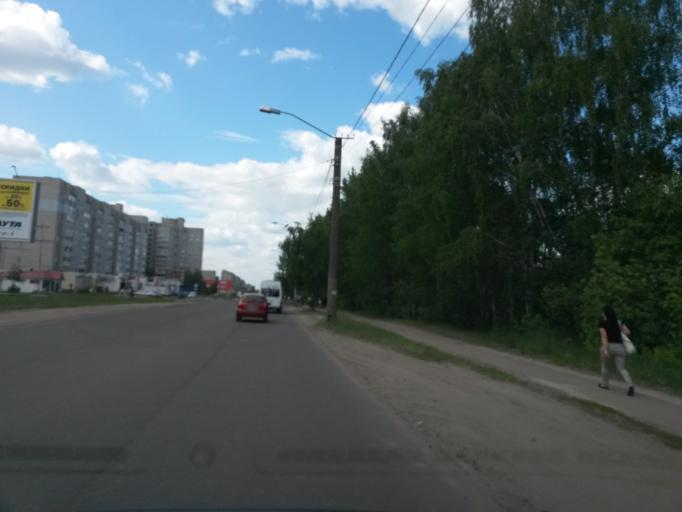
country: RU
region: Jaroslavl
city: Yaroslavl
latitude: 57.6418
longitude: 39.9599
